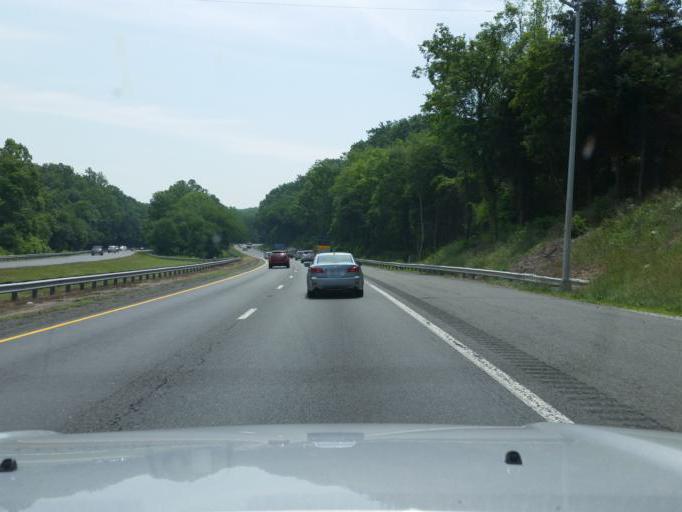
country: US
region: Maryland
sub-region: Frederick County
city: Green Valley
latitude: 39.2746
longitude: -77.3203
